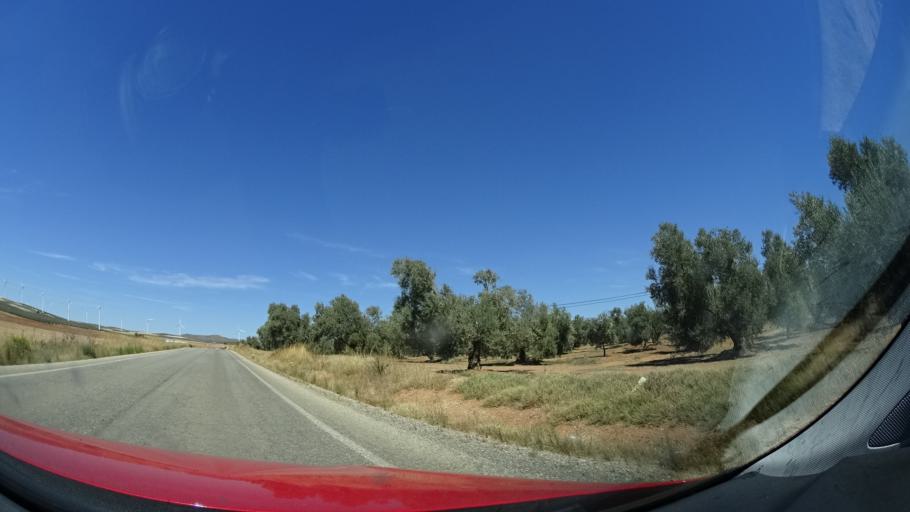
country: ES
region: Andalusia
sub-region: Provincia de Malaga
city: Campillos
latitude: 37.0841
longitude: -4.8666
